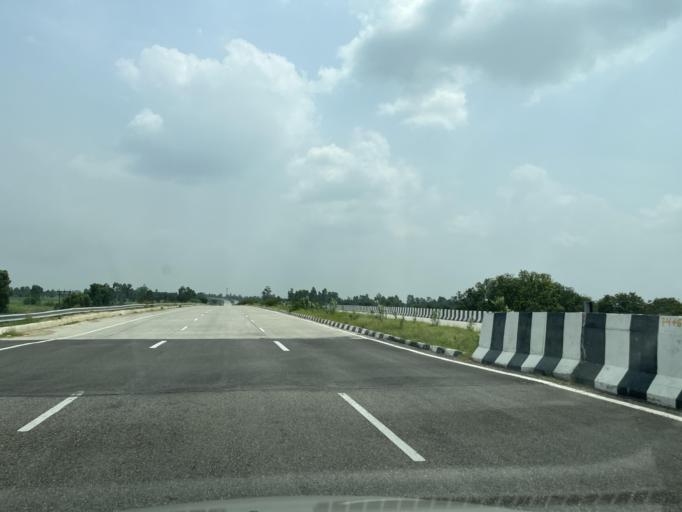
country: IN
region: Uttar Pradesh
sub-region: Bijnor
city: Nagina
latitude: 29.4293
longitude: 78.4169
